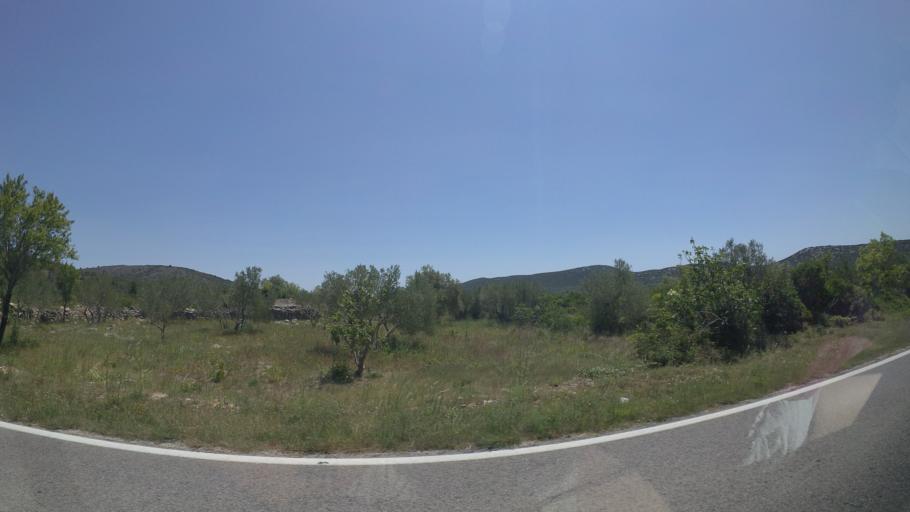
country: HR
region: Sibensko-Kniniska
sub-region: Grad Sibenik
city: Pirovac
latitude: 43.8016
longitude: 15.6923
